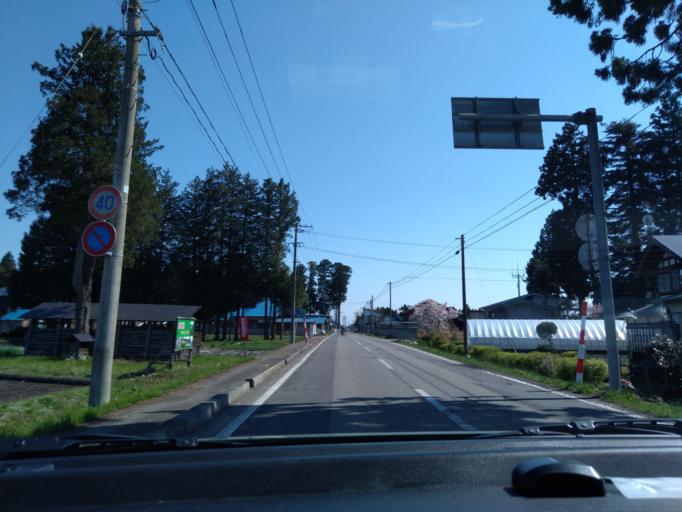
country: JP
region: Akita
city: Kakunodatemachi
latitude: 39.5526
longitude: 140.5860
